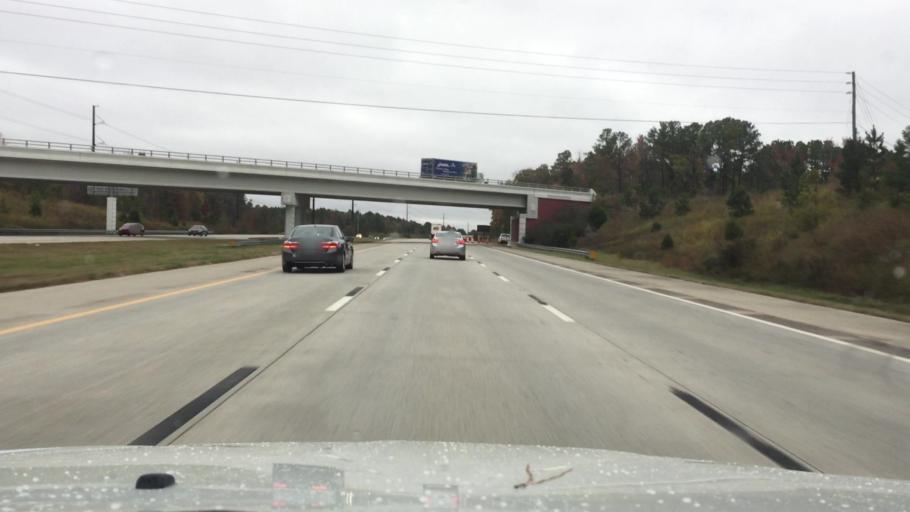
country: US
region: North Carolina
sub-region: Wake County
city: Green Level
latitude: 35.8023
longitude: -78.8910
